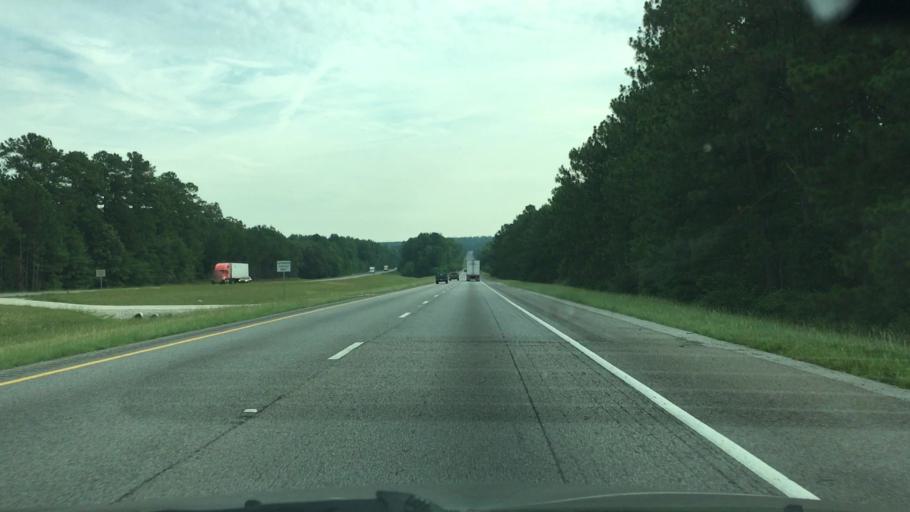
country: US
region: South Carolina
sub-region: Aiken County
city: Aiken
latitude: 33.6882
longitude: -81.6170
